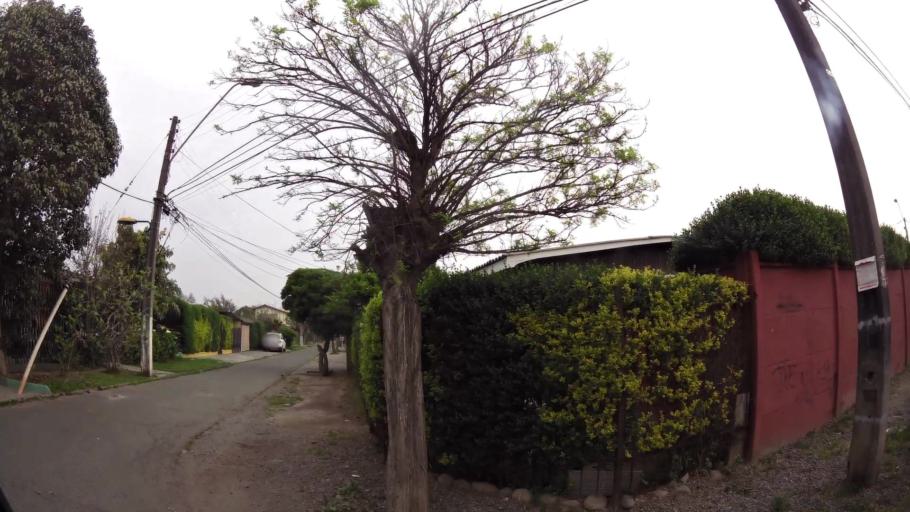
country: CL
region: Santiago Metropolitan
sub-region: Provincia de Santiago
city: Lo Prado
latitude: -33.5140
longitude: -70.7716
